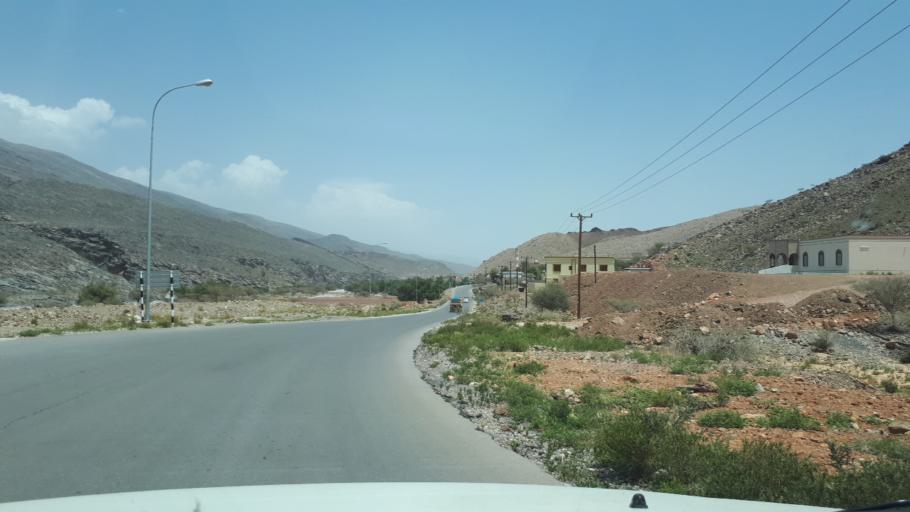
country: OM
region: Muhafazat ad Dakhiliyah
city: Bahla'
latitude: 23.1535
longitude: 57.1841
